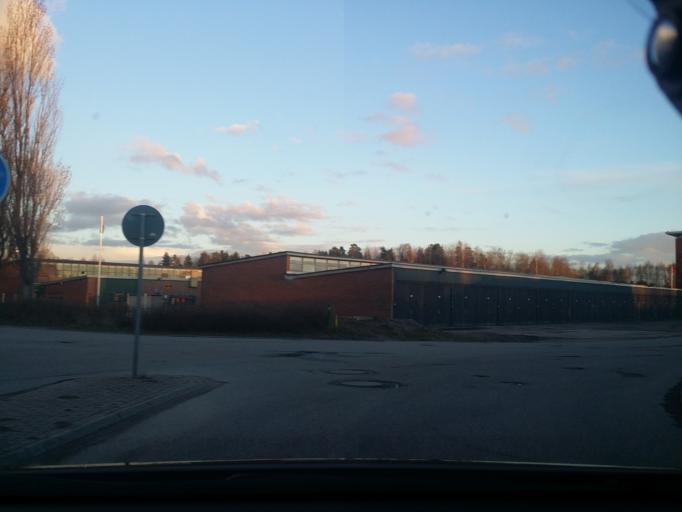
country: SE
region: Vaestmanland
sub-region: Vasteras
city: Vasteras
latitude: 59.6353
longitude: 16.5763
